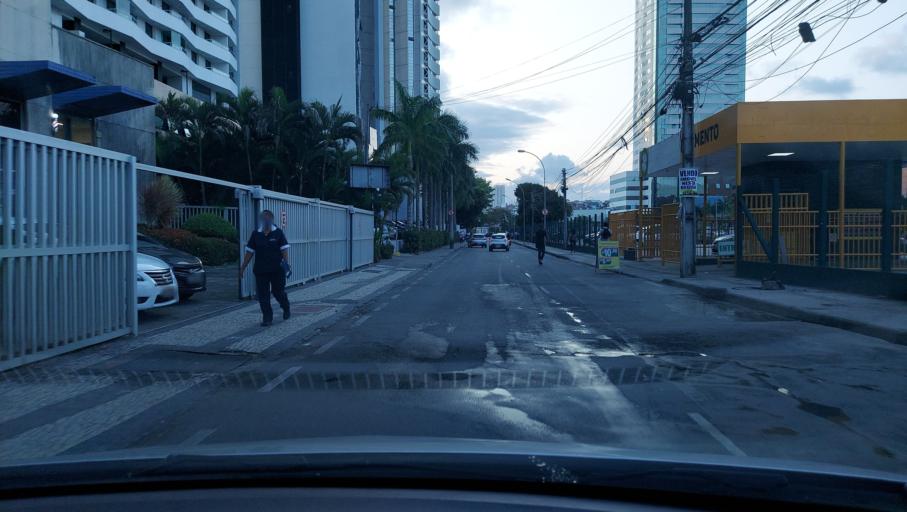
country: BR
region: Bahia
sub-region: Salvador
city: Salvador
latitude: -12.9795
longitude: -38.4560
